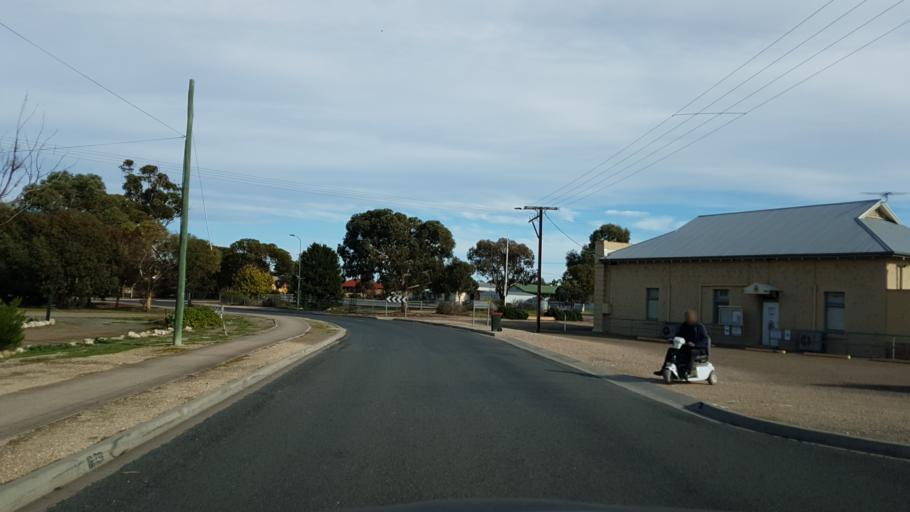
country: AU
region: South Australia
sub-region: Murray Bridge
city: Tailem Bend
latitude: -35.2517
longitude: 139.4565
